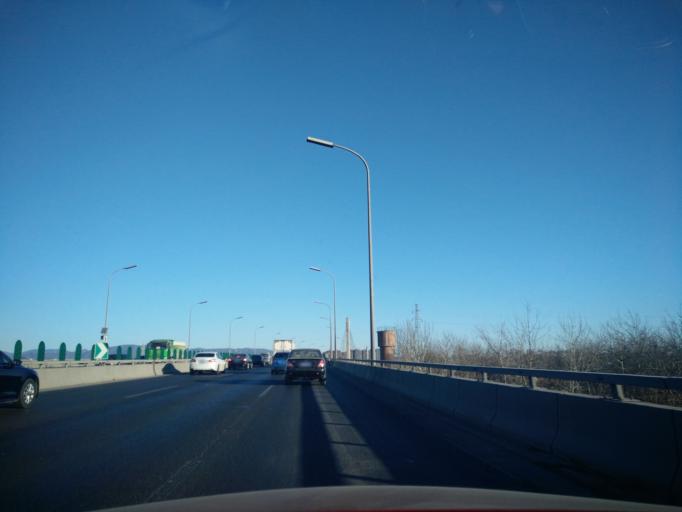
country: CN
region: Beijing
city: Lugu
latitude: 39.8752
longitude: 116.2021
